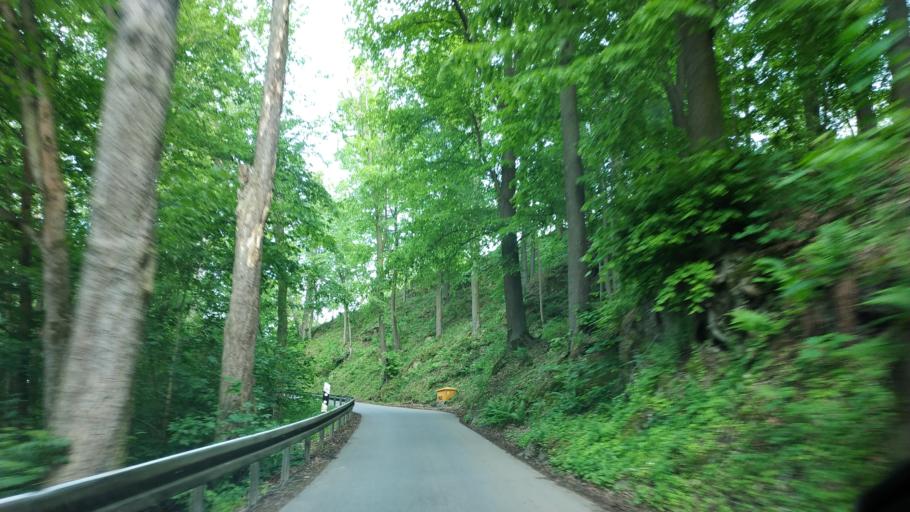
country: DE
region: Saxony
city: Pohl
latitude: 50.5554
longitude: 12.1616
